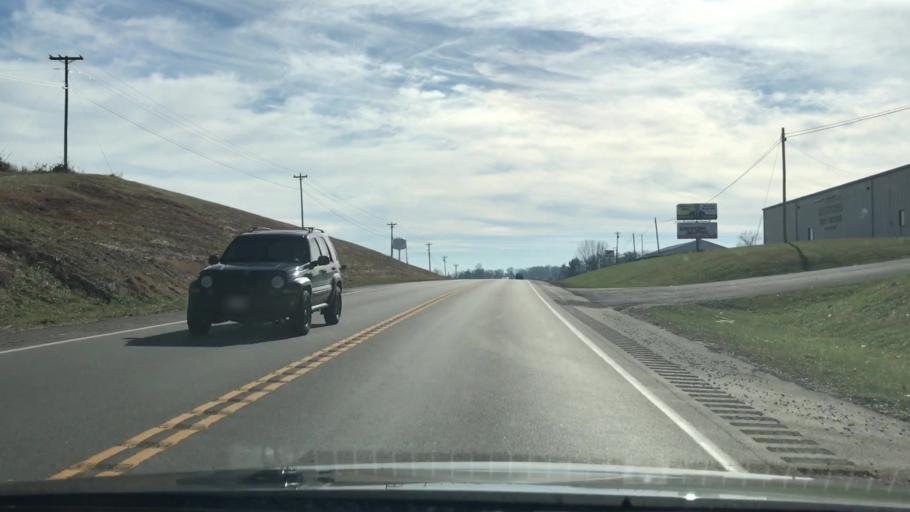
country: US
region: Kentucky
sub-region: Monroe County
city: Tompkinsville
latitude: 36.7326
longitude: -85.6876
